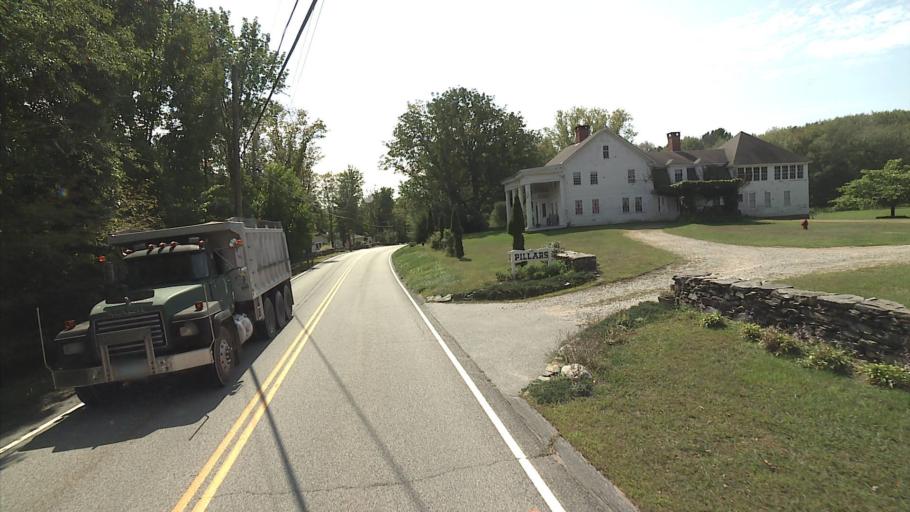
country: US
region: Connecticut
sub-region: Windham County
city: Plainfield Village
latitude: 41.7051
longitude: -71.9682
